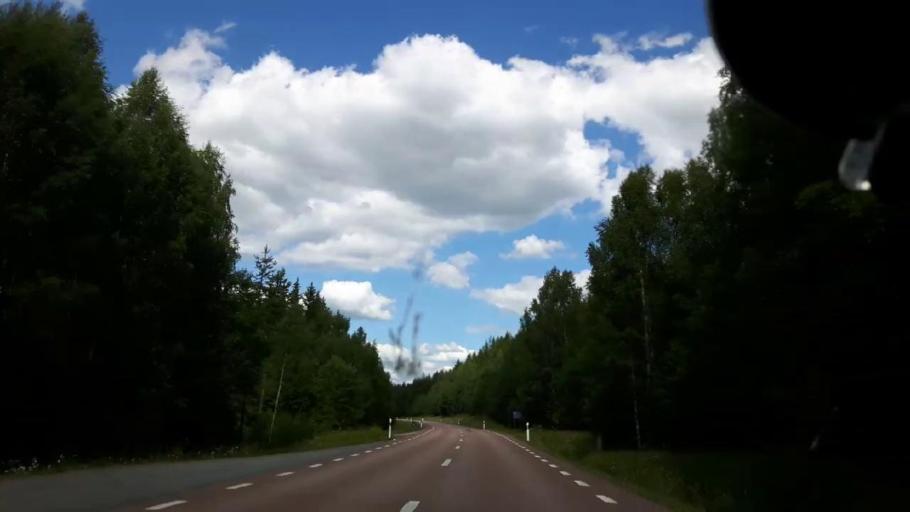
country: SE
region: Jaemtland
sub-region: Ragunda Kommun
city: Hammarstrand
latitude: 62.9200
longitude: 16.7040
